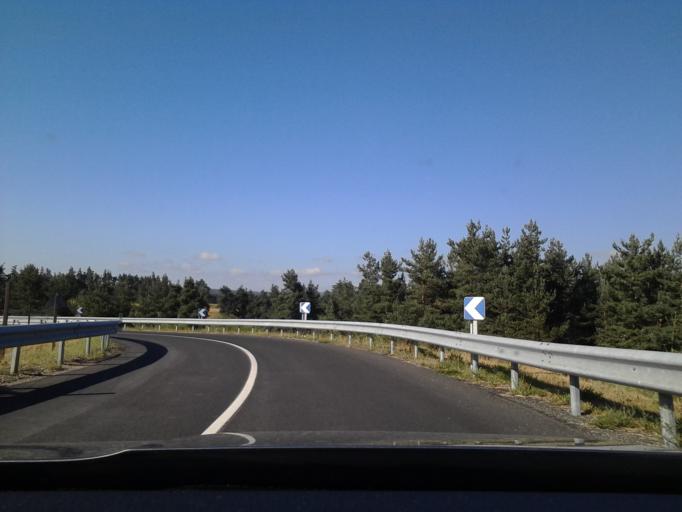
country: FR
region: Languedoc-Roussillon
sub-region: Departement de la Lozere
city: Aumont-Aubrac
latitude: 44.7000
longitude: 3.2818
